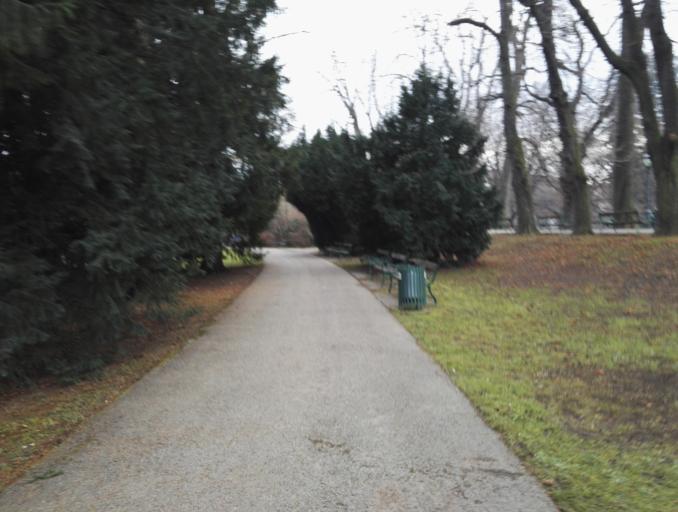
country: AT
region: Styria
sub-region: Graz Stadt
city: Graz
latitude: 47.0753
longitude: 15.4434
